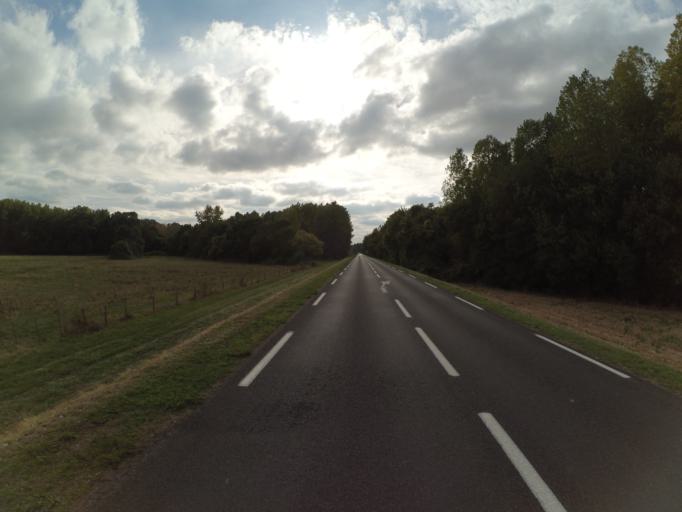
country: FR
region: Centre
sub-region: Departement d'Indre-et-Loire
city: Vernou-sur-Brenne
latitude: 47.4301
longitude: 0.8504
